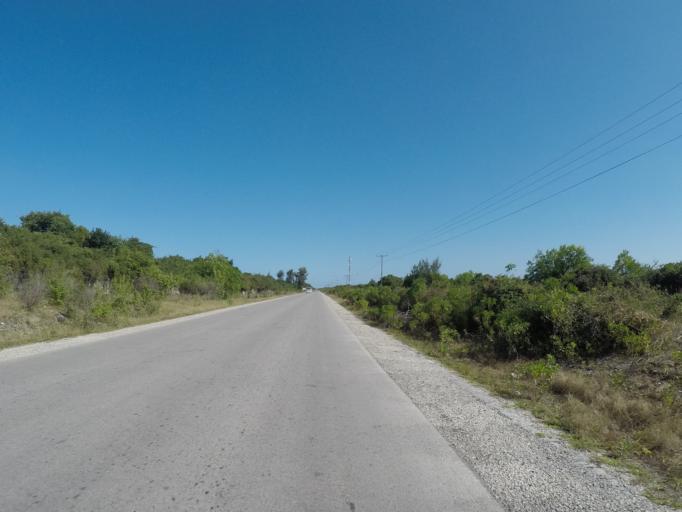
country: TZ
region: Zanzibar Central/South
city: Nganane
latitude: -6.1736
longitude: 39.5267
